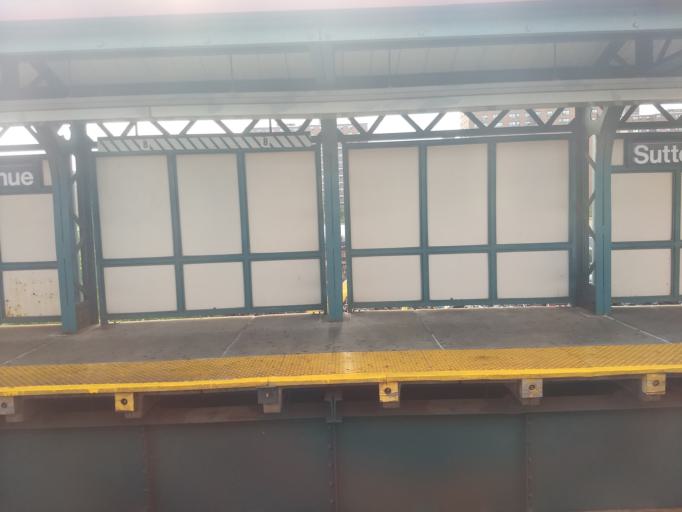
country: US
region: New York
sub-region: Kings County
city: East New York
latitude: 40.6695
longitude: -73.9021
